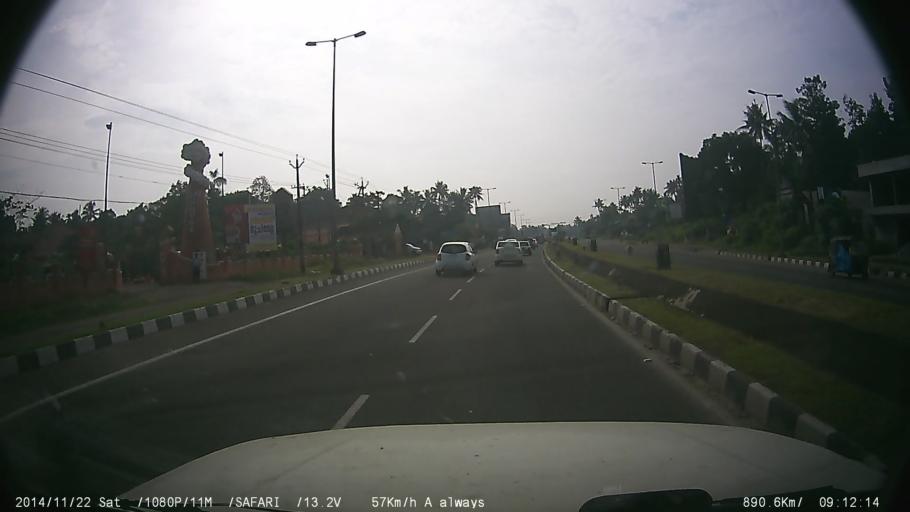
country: IN
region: Kerala
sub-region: Thrissur District
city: Kizhake Chalakudi
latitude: 10.2862
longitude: 76.3418
